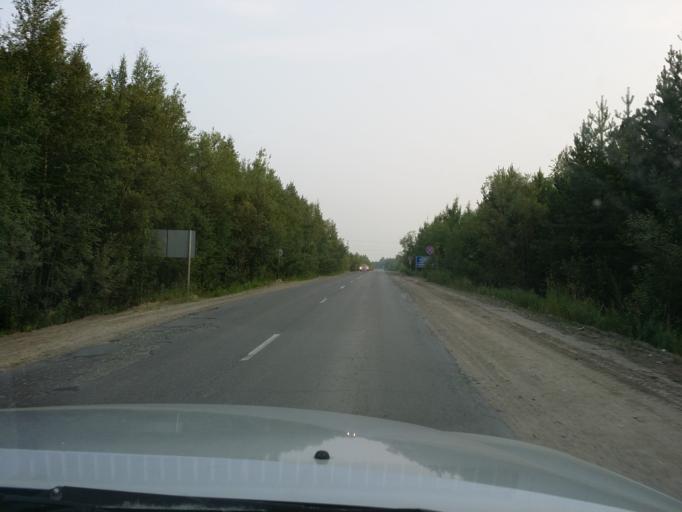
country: RU
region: Khanty-Mansiyskiy Avtonomnyy Okrug
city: Nizhnevartovsk
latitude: 60.9973
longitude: 76.5649
